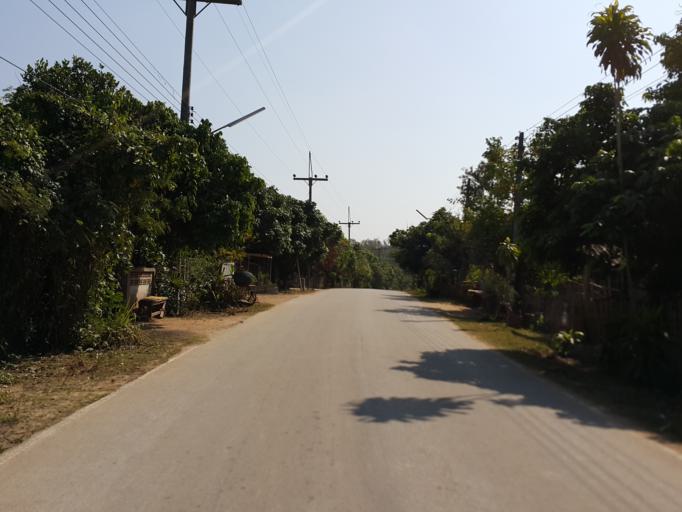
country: TH
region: Lampang
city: Wang Nuea
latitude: 19.0454
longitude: 99.6238
